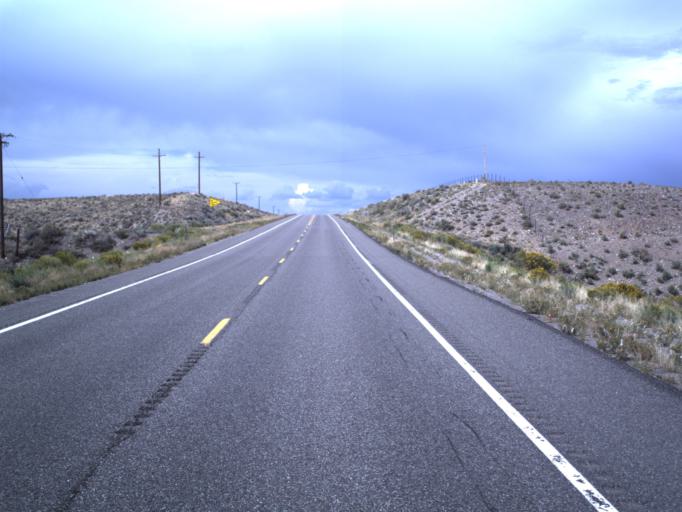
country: US
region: Utah
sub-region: Piute County
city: Junction
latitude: 38.4120
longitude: -112.2313
